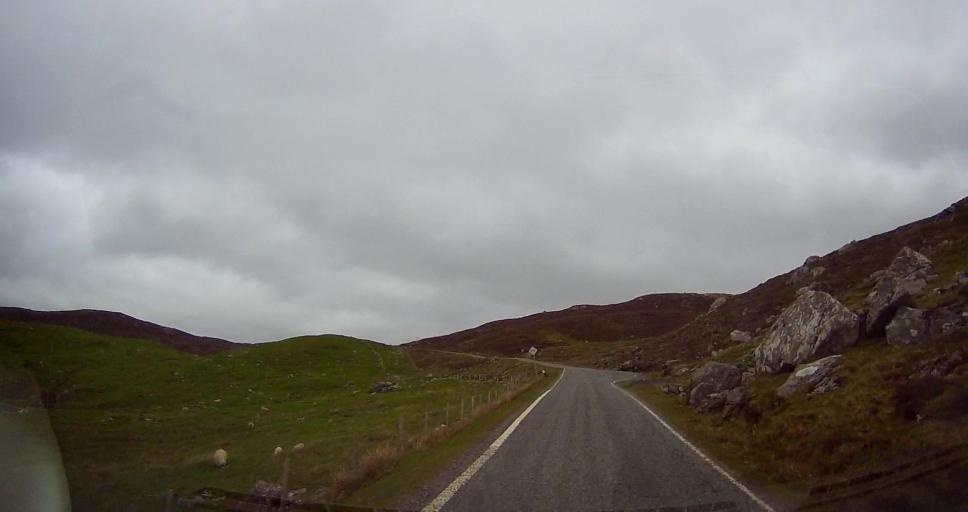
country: GB
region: Scotland
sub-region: Shetland Islands
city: Lerwick
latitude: 60.3363
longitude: -1.3249
